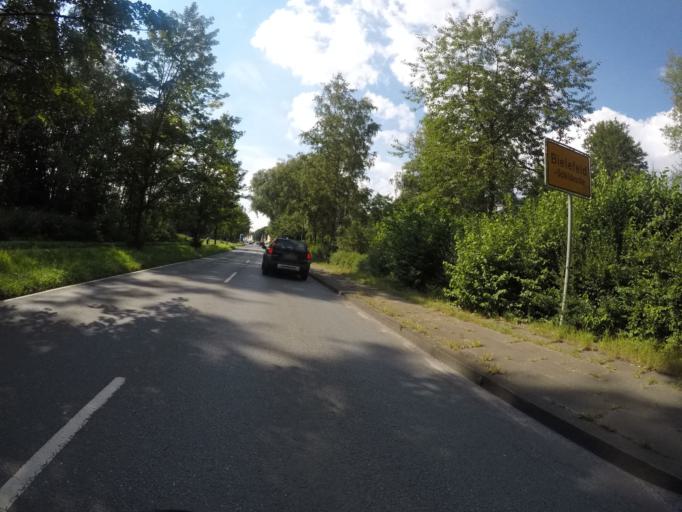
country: DE
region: North Rhine-Westphalia
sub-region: Regierungsbezirk Detmold
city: Bielefeld
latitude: 52.0541
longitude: 8.5686
